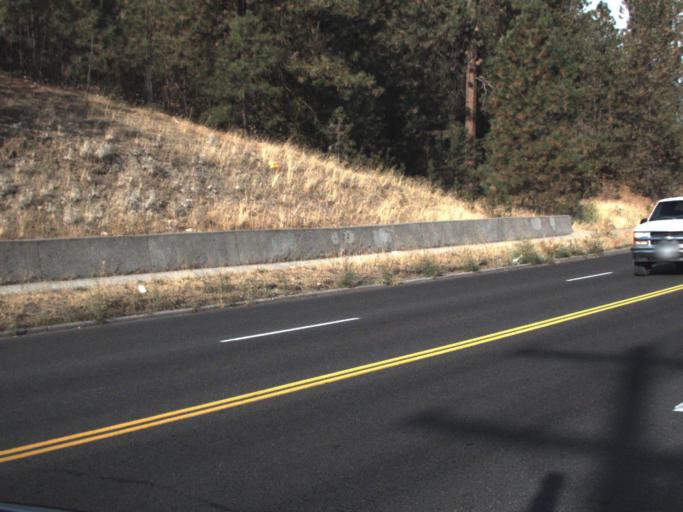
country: US
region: Washington
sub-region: Spokane County
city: Town and Country
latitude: 47.7169
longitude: -117.4793
